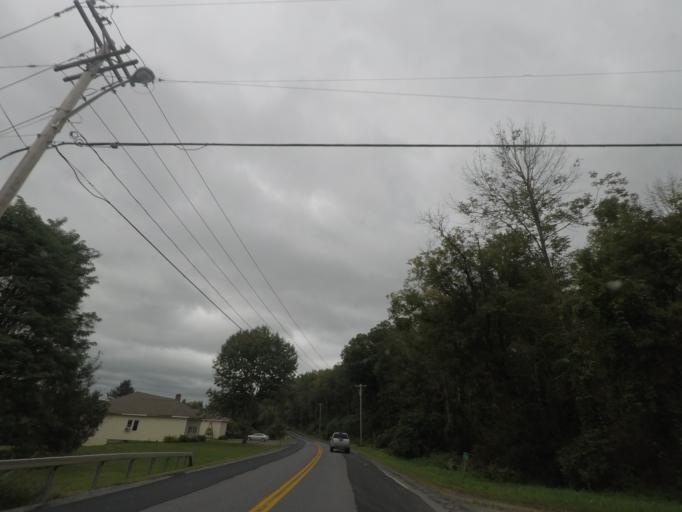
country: US
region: New York
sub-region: Rensselaer County
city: Hoosick Falls
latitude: 42.9503
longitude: -73.4050
